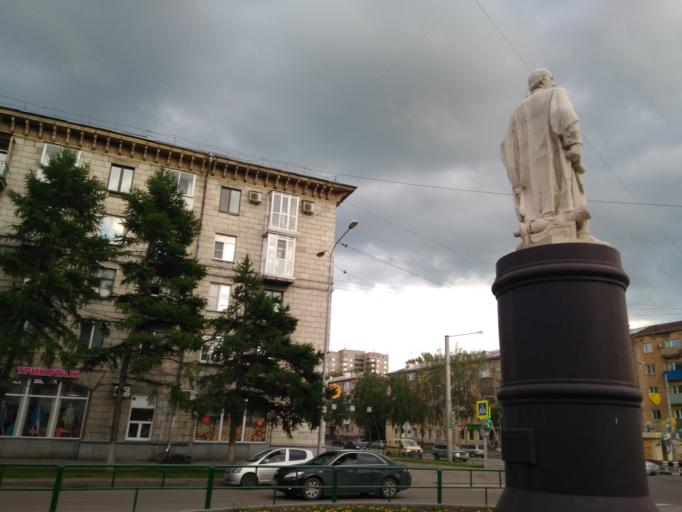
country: RU
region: Kemerovo
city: Novokuznetsk
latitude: 53.7547
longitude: 87.1092
